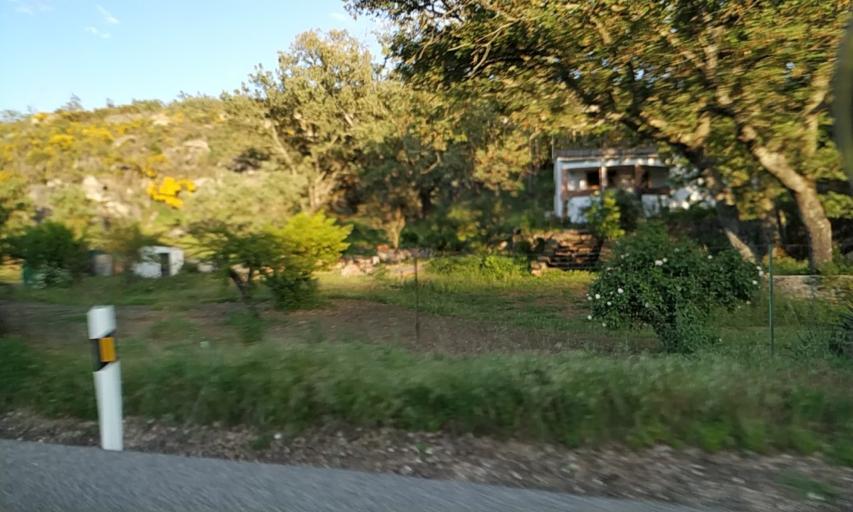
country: ES
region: Extremadura
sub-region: Provincia de Caceres
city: Valencia de Alcantara
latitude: 39.3688
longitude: -7.2666
